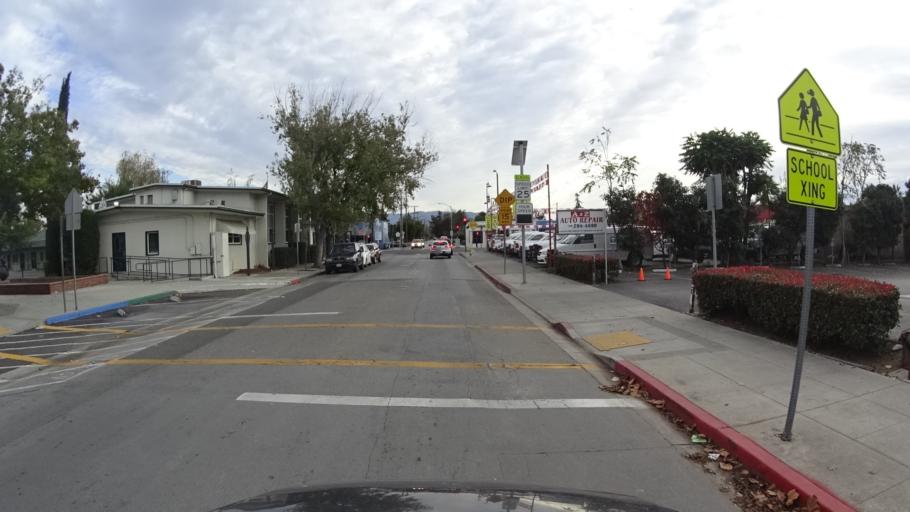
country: US
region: California
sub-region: Santa Clara County
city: Burbank
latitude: 37.3241
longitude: -121.9268
